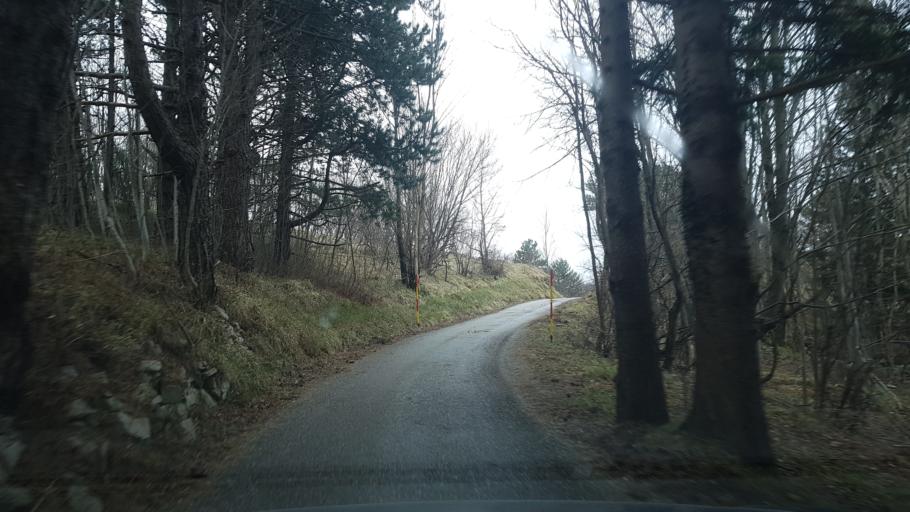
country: SI
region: Nova Gorica
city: Kromberk
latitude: 46.0243
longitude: 13.7025
